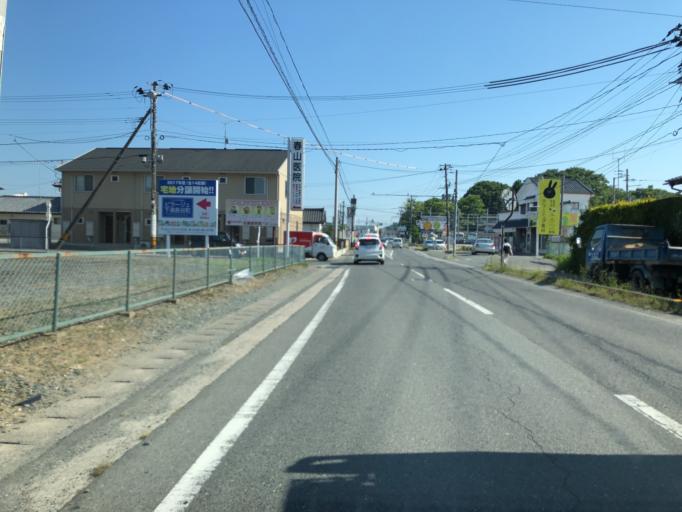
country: JP
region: Fukushima
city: Iwaki
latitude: 36.9917
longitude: 140.8539
